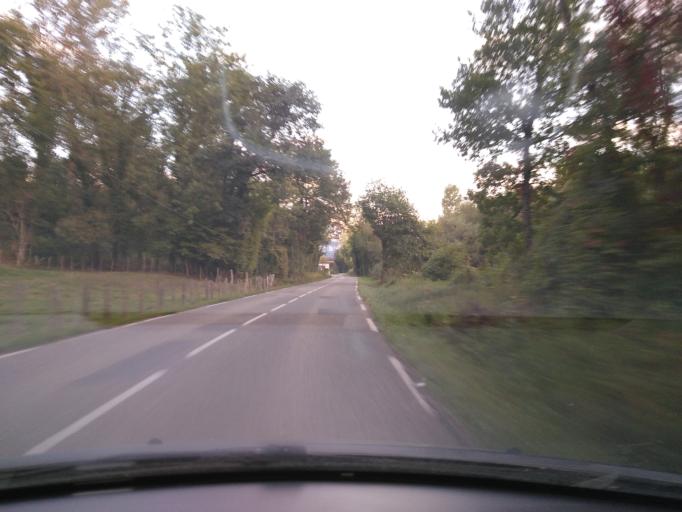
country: FR
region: Rhone-Alpes
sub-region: Departement de l'Isere
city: La Murette
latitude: 45.3686
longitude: 5.5427
